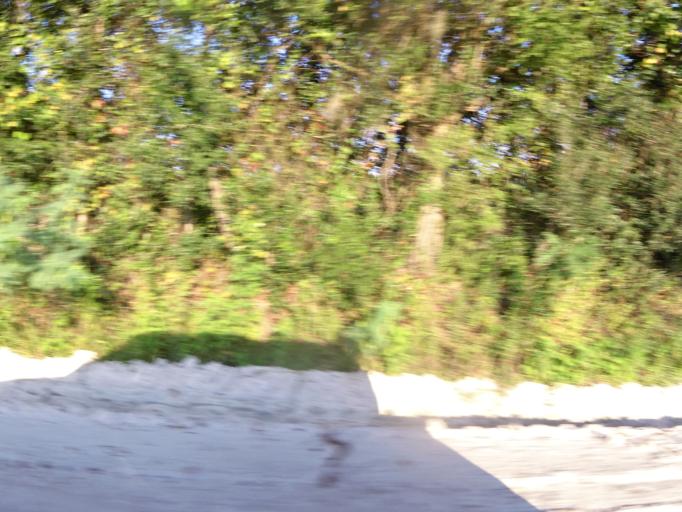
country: US
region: Florida
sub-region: Nassau County
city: Callahan
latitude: 30.5403
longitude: -81.9980
